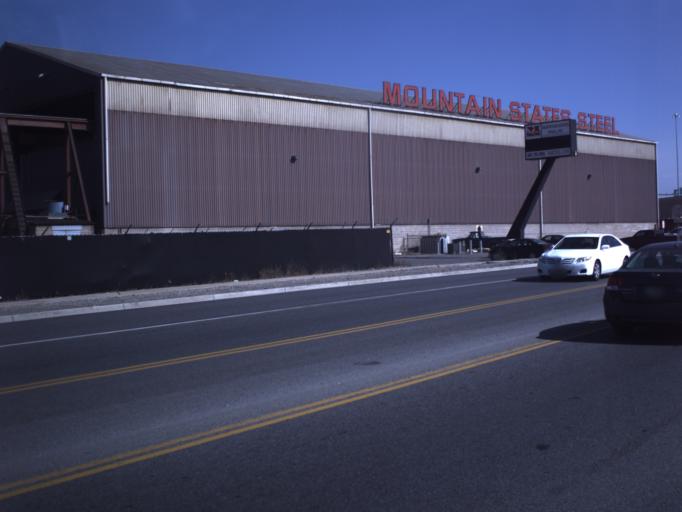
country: US
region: Utah
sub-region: Utah County
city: Lindon
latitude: 40.3321
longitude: -111.7385
